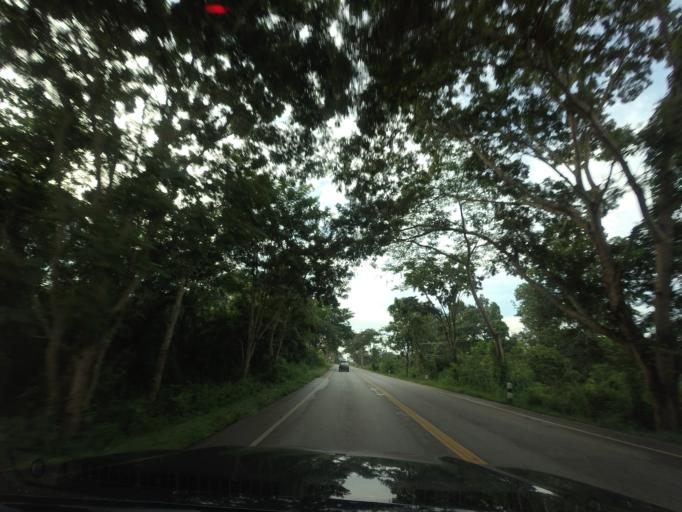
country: TH
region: Changwat Udon Thani
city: Nam Som
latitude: 17.8359
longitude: 102.2601
